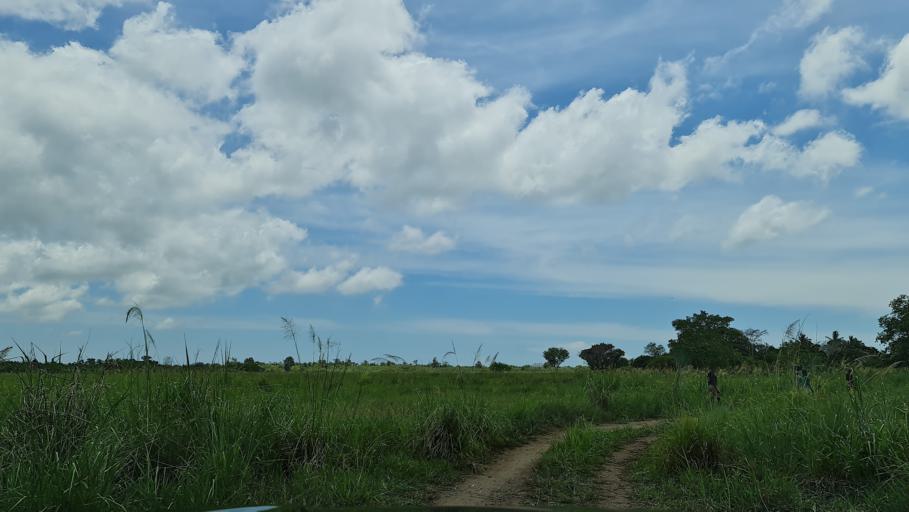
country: MZ
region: Zambezia
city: Quelimane
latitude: -17.5856
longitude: 37.3944
